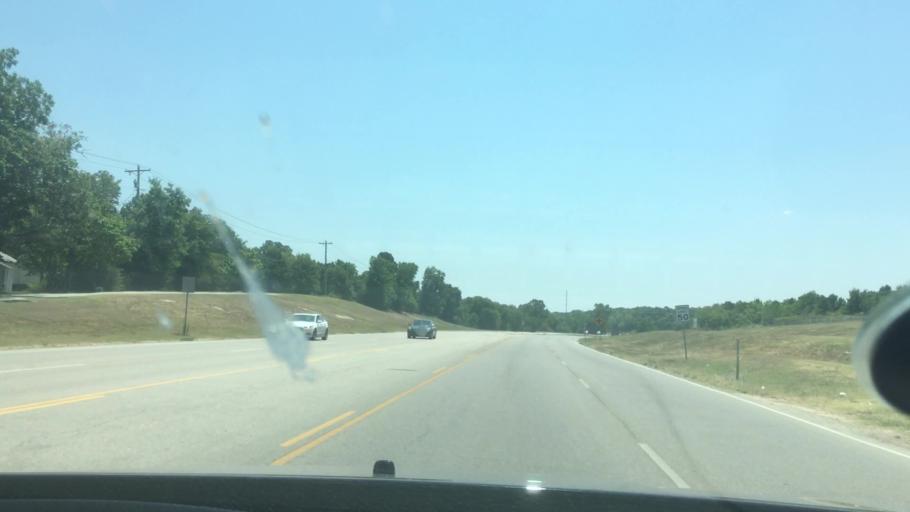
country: US
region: Oklahoma
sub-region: Pontotoc County
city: Ada
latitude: 34.7564
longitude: -96.6597
